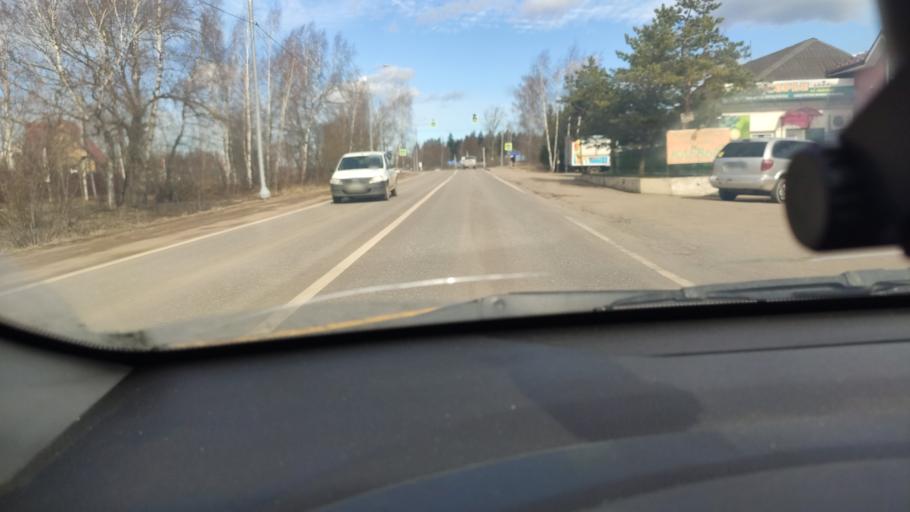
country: RU
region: Moskovskaya
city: Ruza
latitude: 55.7584
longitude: 36.1445
